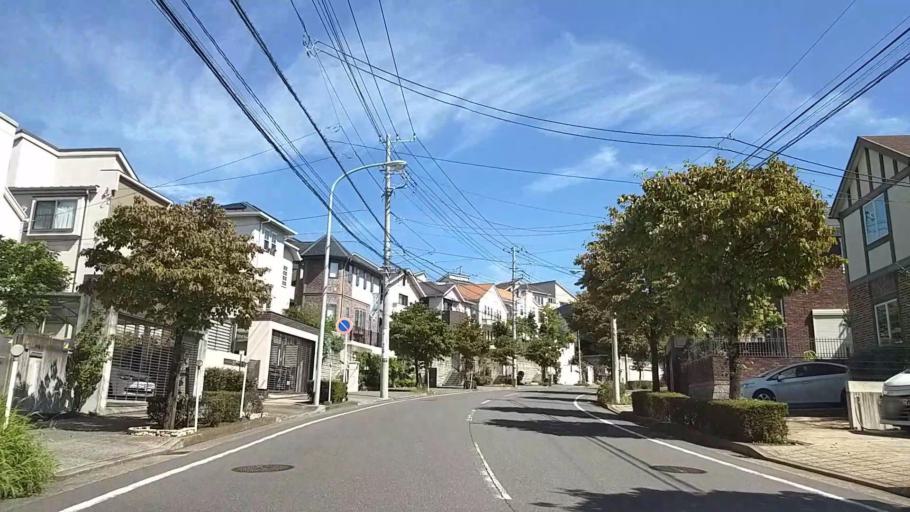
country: JP
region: Tokyo
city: Chofugaoka
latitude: 35.5634
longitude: 139.5490
